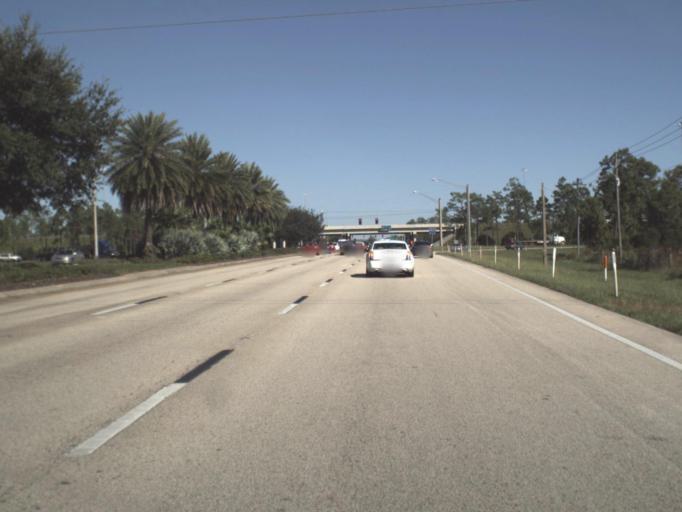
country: US
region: Florida
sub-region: Lee County
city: Gateway
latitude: 26.5472
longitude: -81.7984
